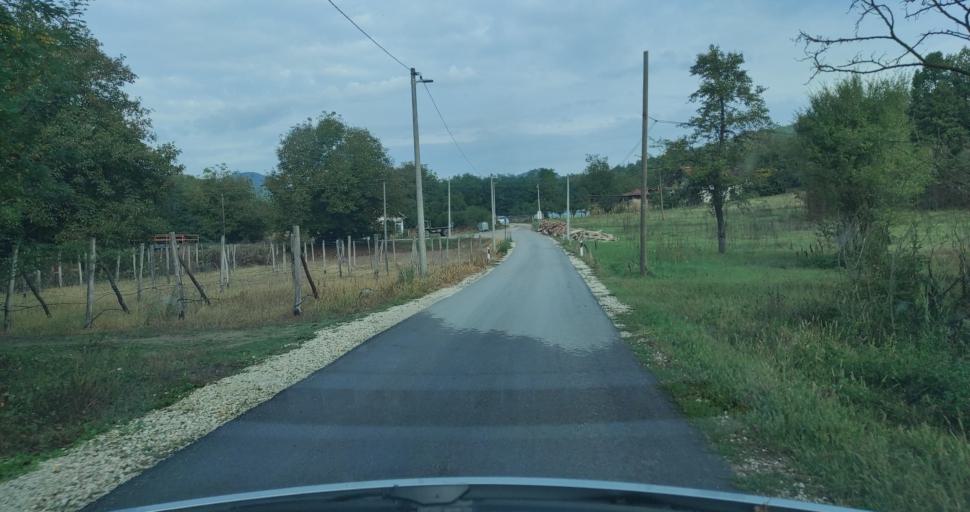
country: RS
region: Central Serbia
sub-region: Pcinjski Okrug
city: Vladicin Han
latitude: 42.6735
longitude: 22.0190
